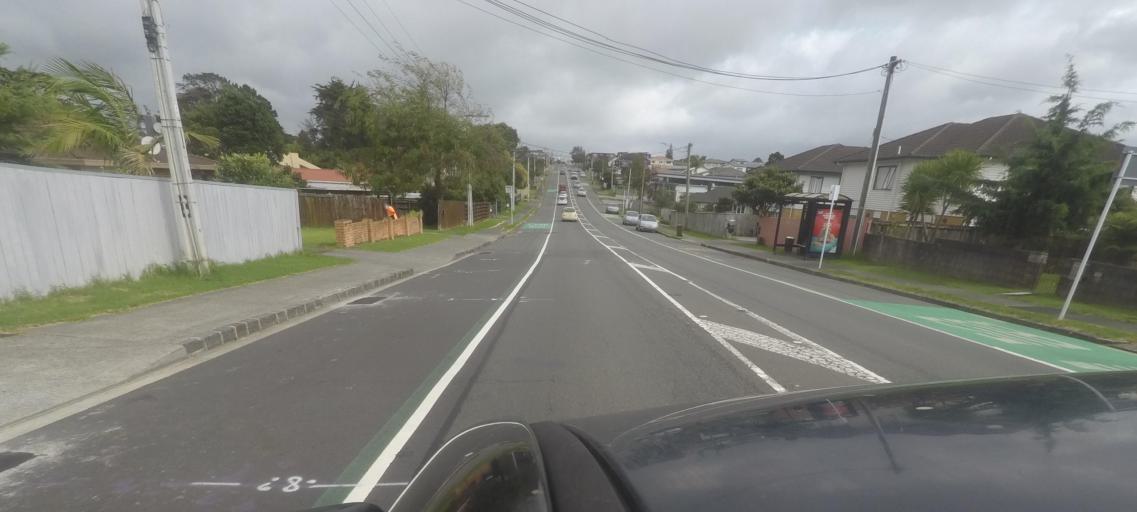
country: NZ
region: Auckland
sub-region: Auckland
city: Auckland
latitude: -36.9148
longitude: 174.7384
